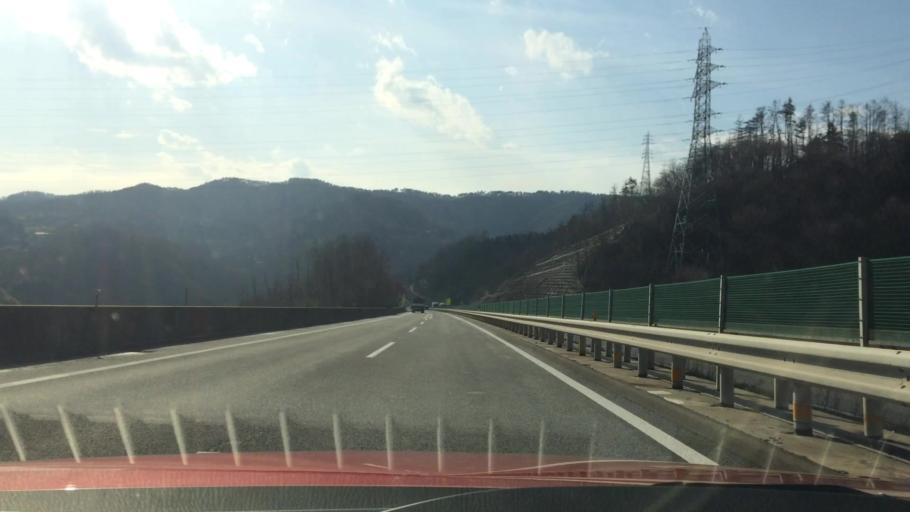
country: JP
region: Nagano
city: Toyoshina
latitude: 36.3510
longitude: 137.9674
